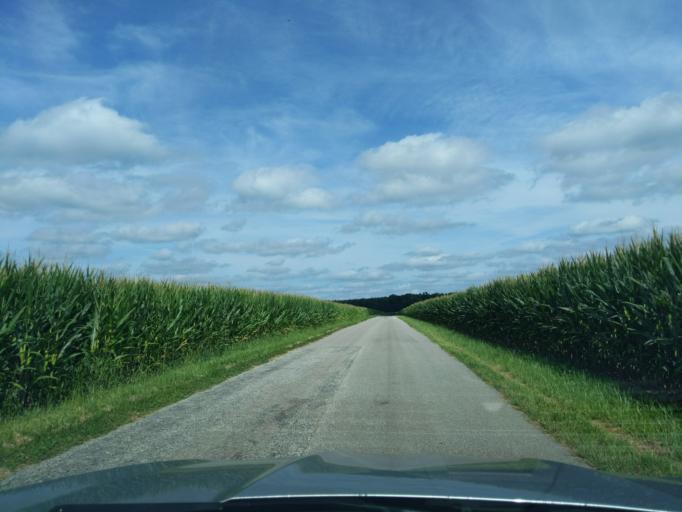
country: US
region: Indiana
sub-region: Ripley County
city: Osgood
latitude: 39.2354
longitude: -85.3678
